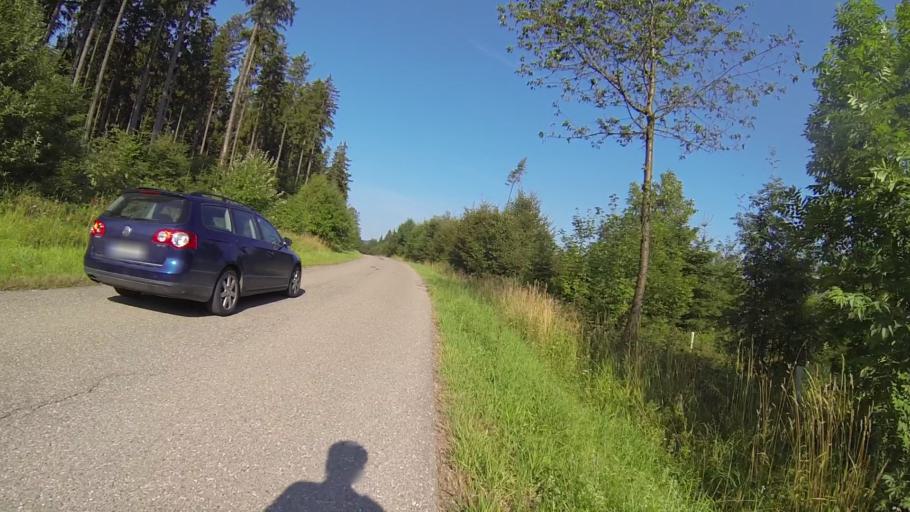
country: DE
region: Baden-Wuerttemberg
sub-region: Regierungsbezirk Stuttgart
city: Konigsbronn
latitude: 48.7516
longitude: 10.1277
